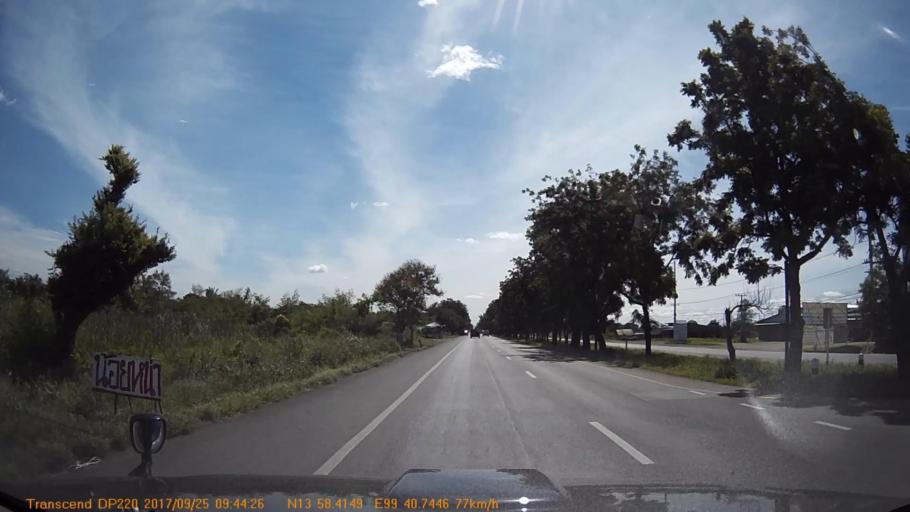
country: TH
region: Kanchanaburi
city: Tha Muang
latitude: 13.9735
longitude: 99.6794
